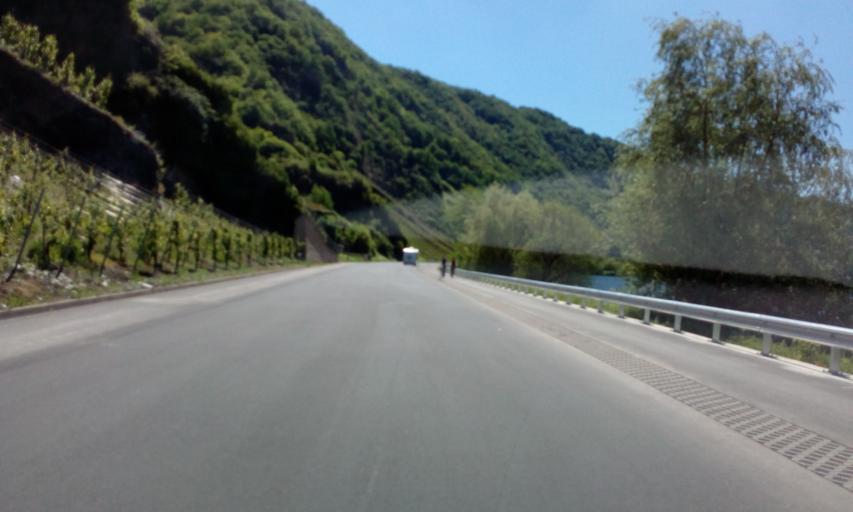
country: DE
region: Rheinland-Pfalz
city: Minheim
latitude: 49.8701
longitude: 6.9485
